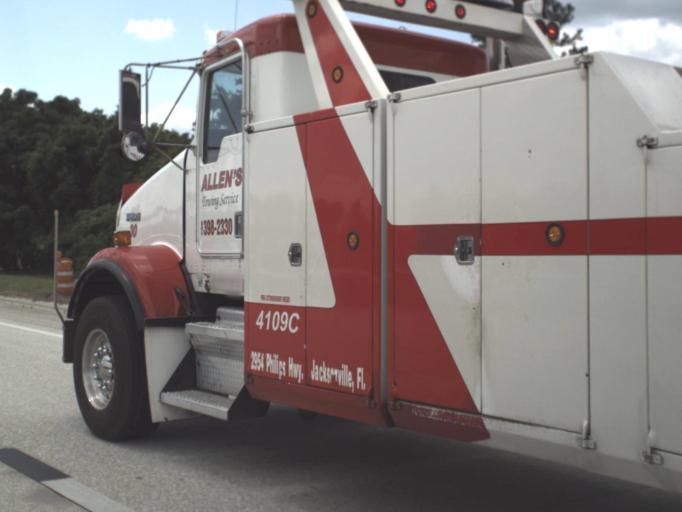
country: US
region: Florida
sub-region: Saint Johns County
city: Fruit Cove
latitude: 30.1664
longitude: -81.5489
